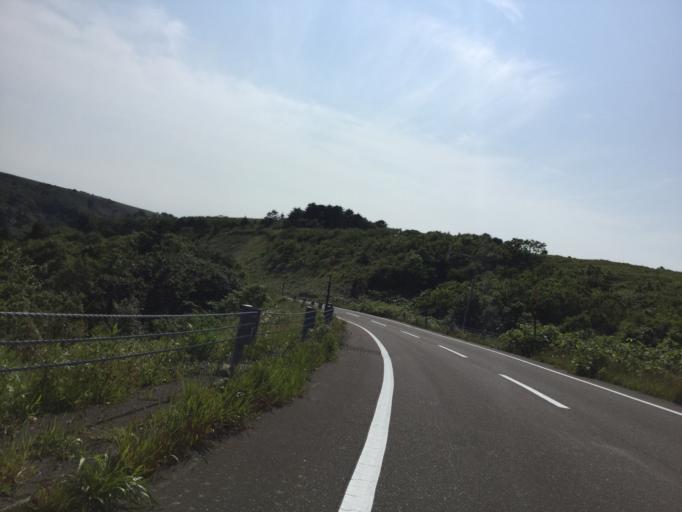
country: JP
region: Hokkaido
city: Makubetsu
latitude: 45.4991
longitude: 141.9096
